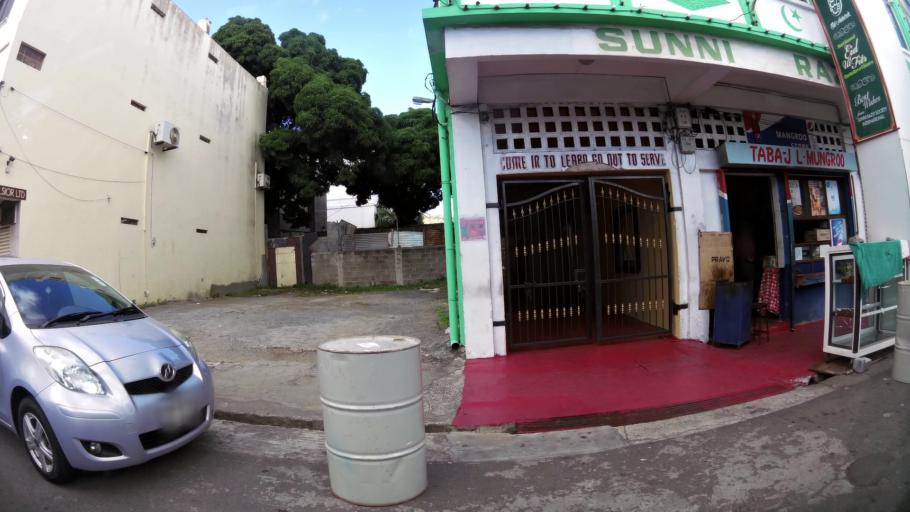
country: MU
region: Port Louis
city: Port Louis
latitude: -20.1572
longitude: 57.5093
